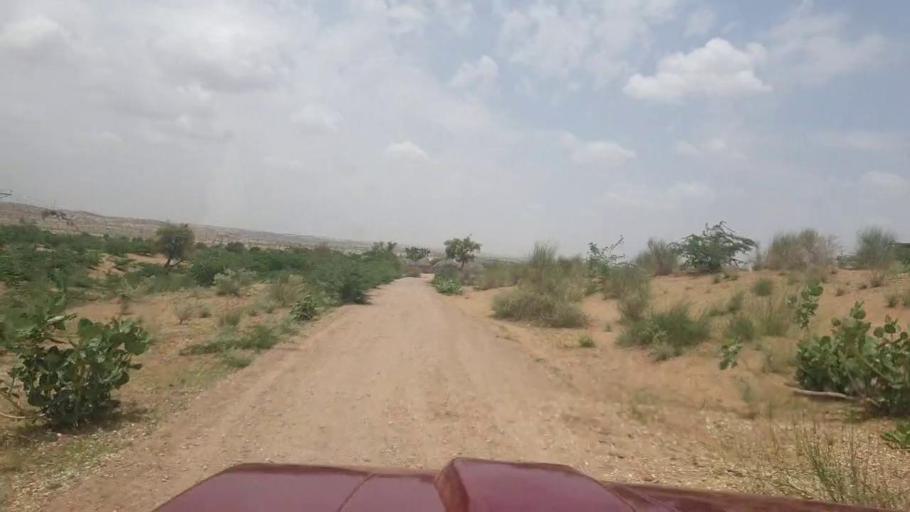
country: PK
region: Sindh
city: Islamkot
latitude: 25.2282
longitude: 70.5076
